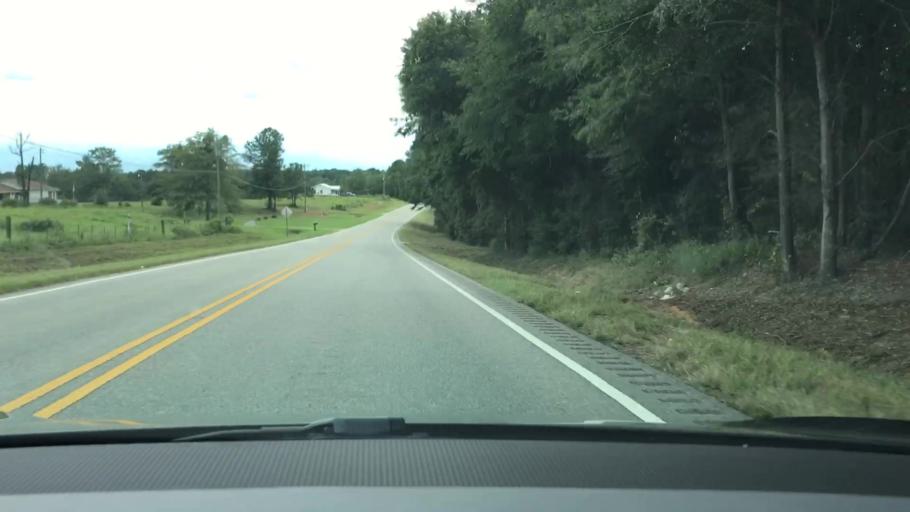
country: US
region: Alabama
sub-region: Pike County
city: Troy
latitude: 31.6606
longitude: -85.9607
